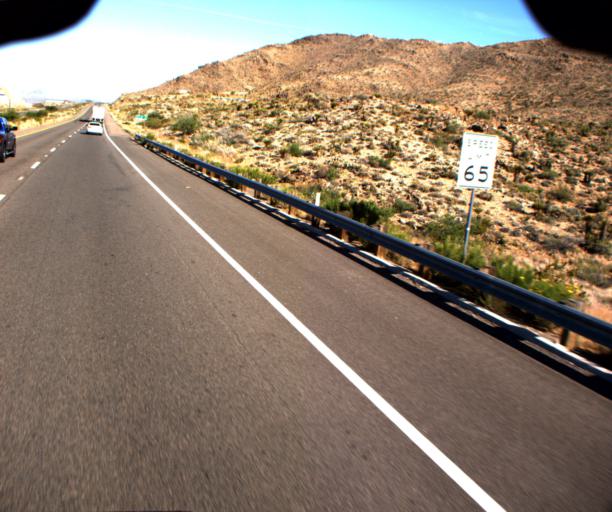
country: US
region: Arizona
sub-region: Mohave County
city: Kingman
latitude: 35.2224
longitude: -114.1269
